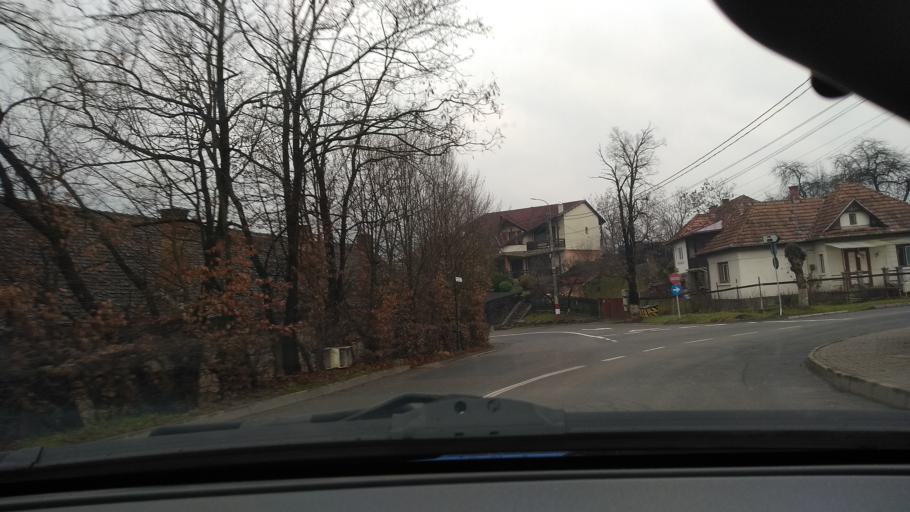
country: RO
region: Mures
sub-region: Oras Sovata
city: Sovata
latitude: 46.5968
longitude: 25.0747
